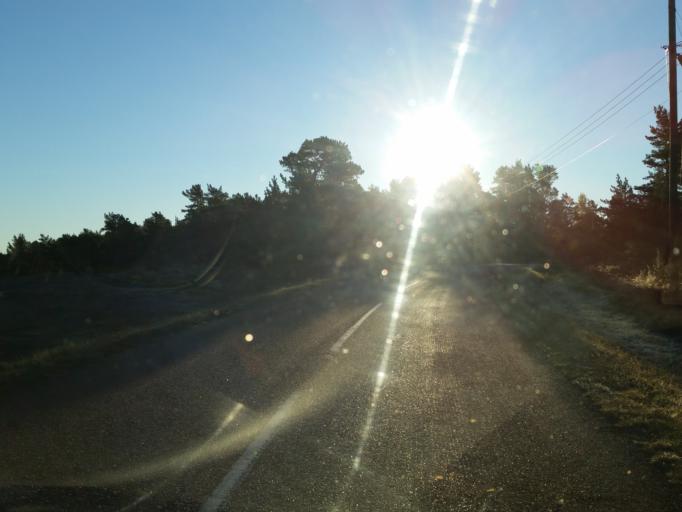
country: AX
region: Alands skaergard
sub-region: Vardoe
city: Vardoe
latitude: 60.3091
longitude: 20.3784
